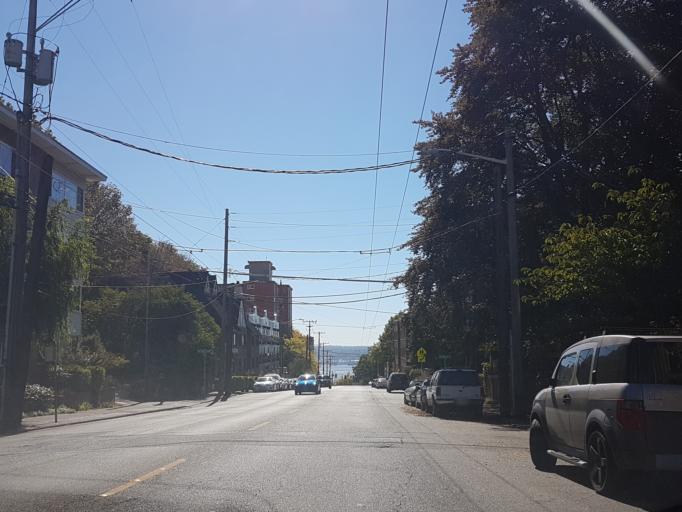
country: US
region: Washington
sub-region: King County
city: Seattle
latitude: 47.6318
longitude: -122.3566
